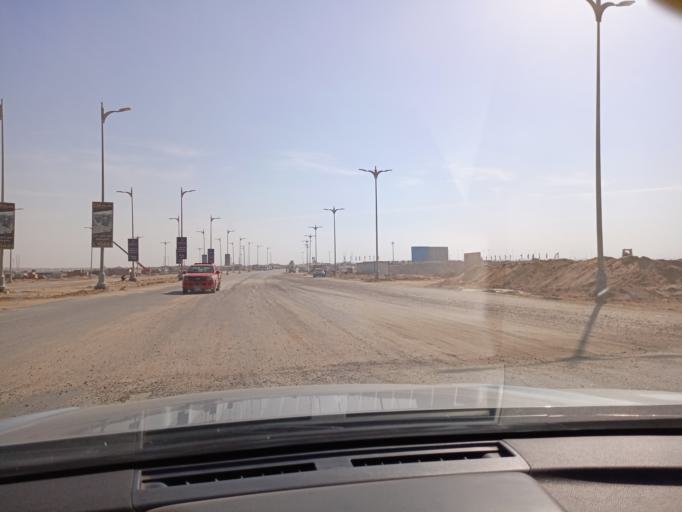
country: EG
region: Muhafazat al Qalyubiyah
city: Al Khankah
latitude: 30.0271
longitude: 31.6788
